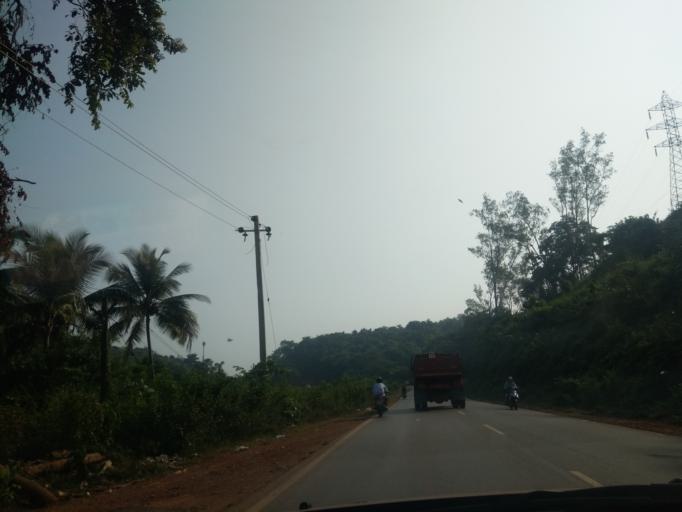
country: IN
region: Goa
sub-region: North Goa
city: Curti
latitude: 15.4137
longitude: 74.0325
